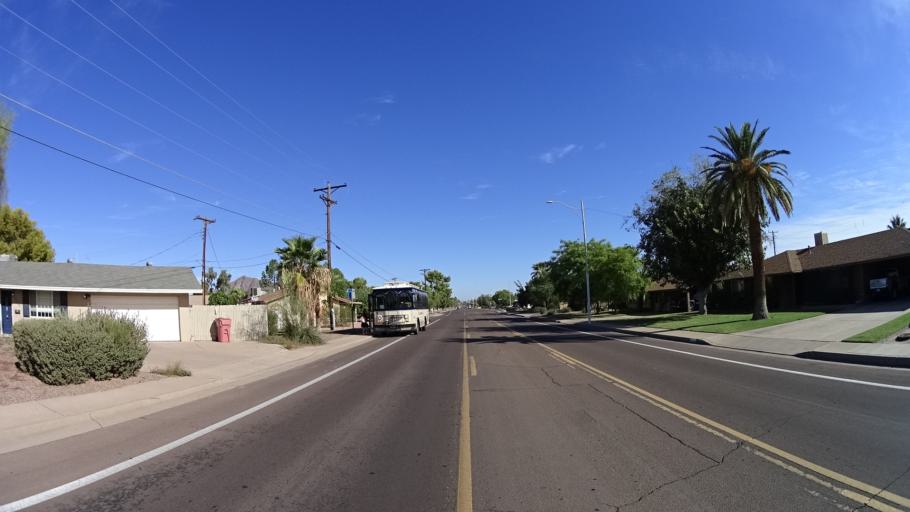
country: US
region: Arizona
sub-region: Maricopa County
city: Scottsdale
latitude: 33.4755
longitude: -111.9348
